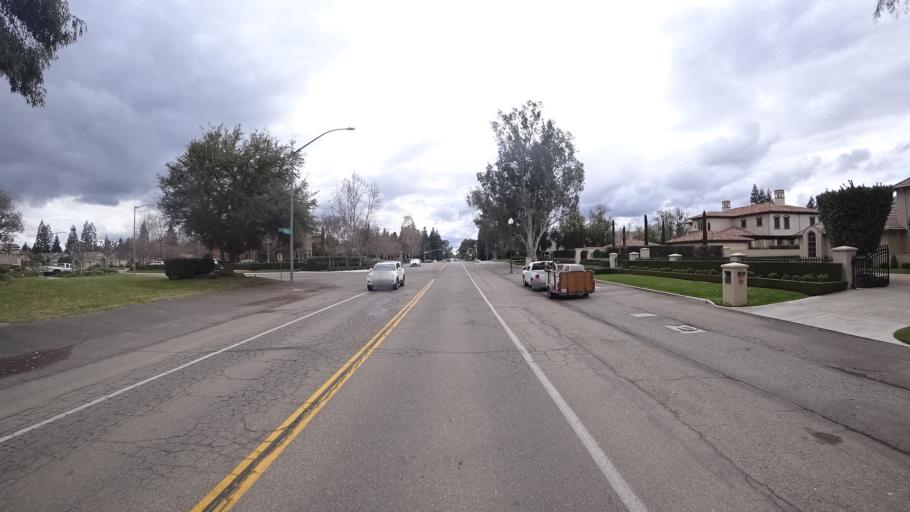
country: US
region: California
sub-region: Fresno County
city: Fresno
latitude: 36.8389
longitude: -119.8355
